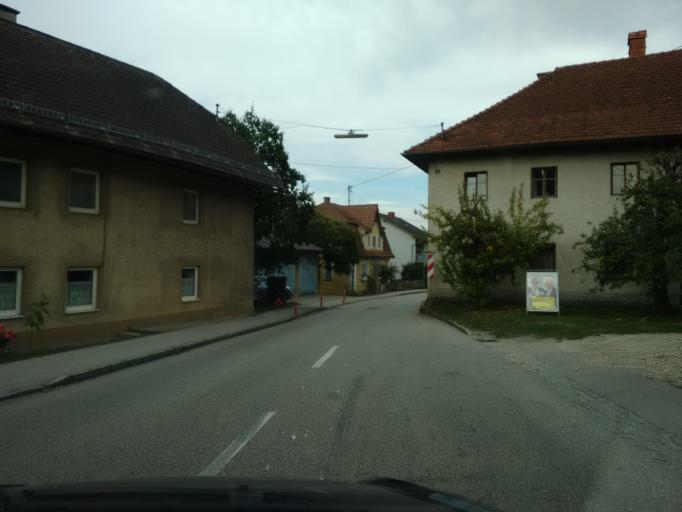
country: AT
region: Upper Austria
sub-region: Wels-Land
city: Marchtrenk
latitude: 48.1645
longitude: 14.1286
